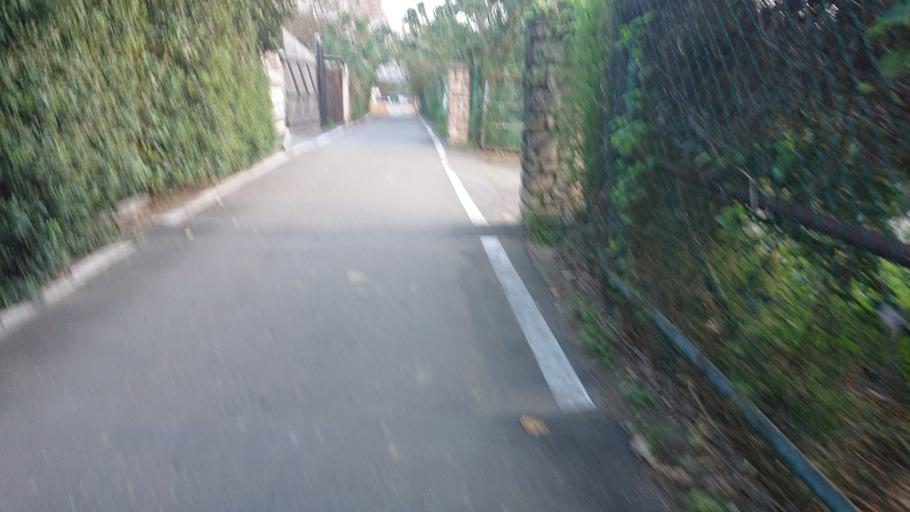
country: TW
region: Taipei
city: Taipei
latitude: 25.1891
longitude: 121.4182
